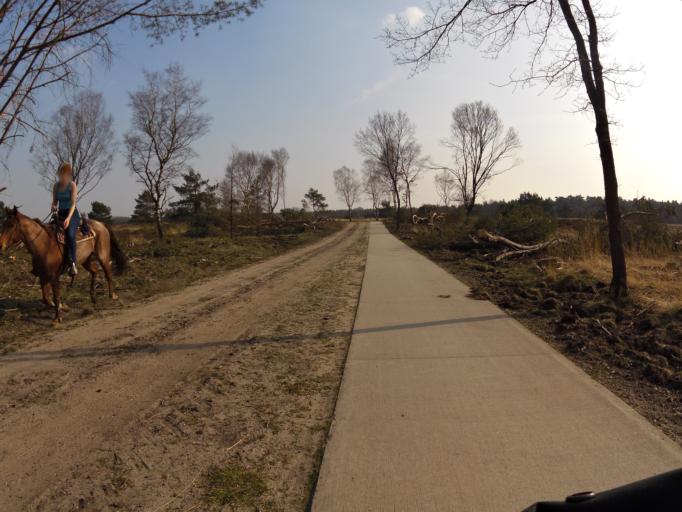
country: NL
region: Gelderland
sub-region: Gemeente Epe
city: Emst
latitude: 52.3236
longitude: 5.8869
